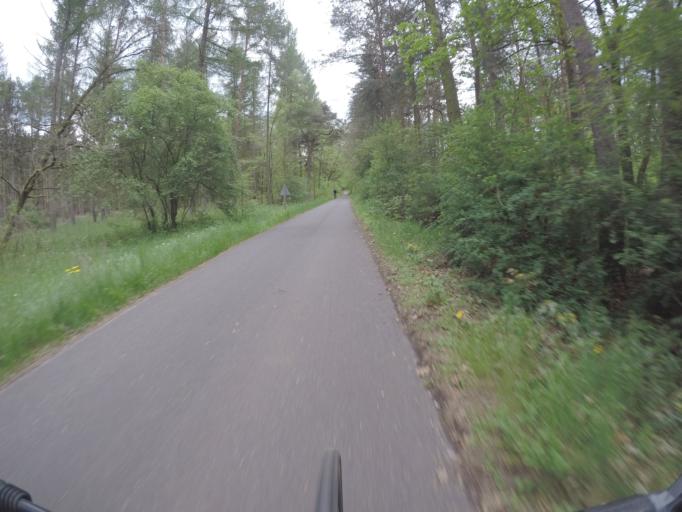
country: DE
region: Brandenburg
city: Marienwerder
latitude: 52.8353
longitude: 13.6259
